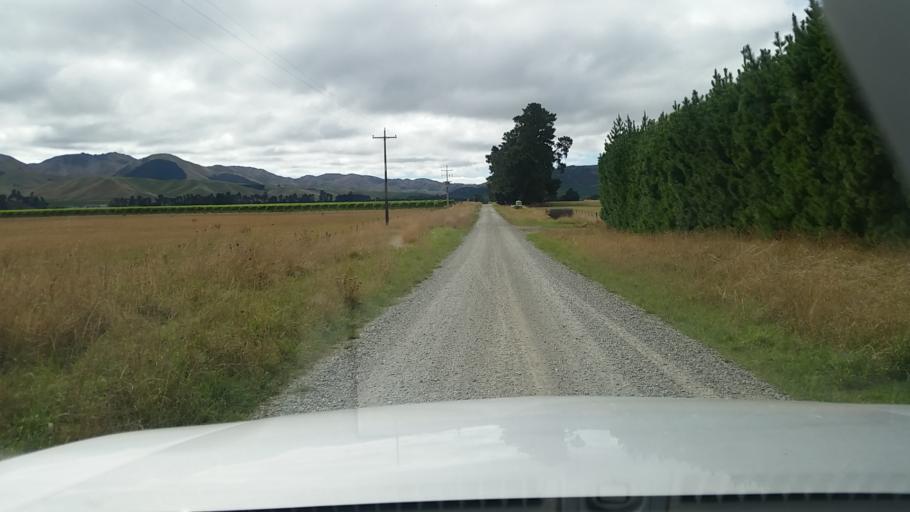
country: NZ
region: Marlborough
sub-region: Marlborough District
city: Blenheim
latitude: -41.6774
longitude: 174.0386
